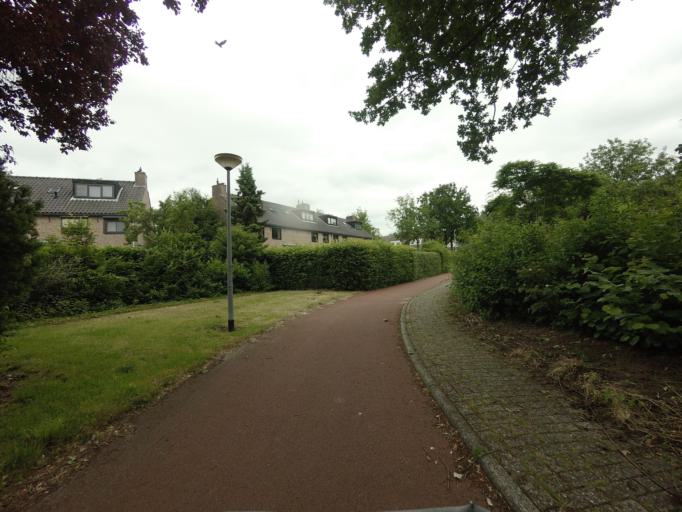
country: NL
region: North Holland
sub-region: Gemeente Huizen
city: Huizen
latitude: 52.2899
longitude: 5.2669
